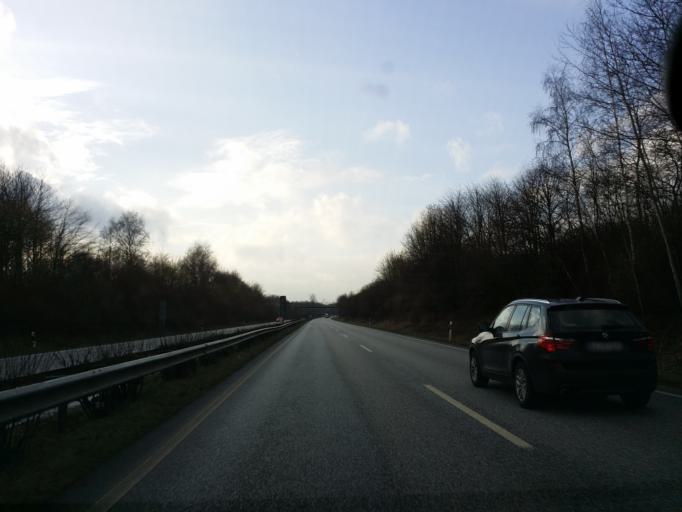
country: DE
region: Schleswig-Holstein
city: Krummwisch
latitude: 54.3138
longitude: 9.9006
